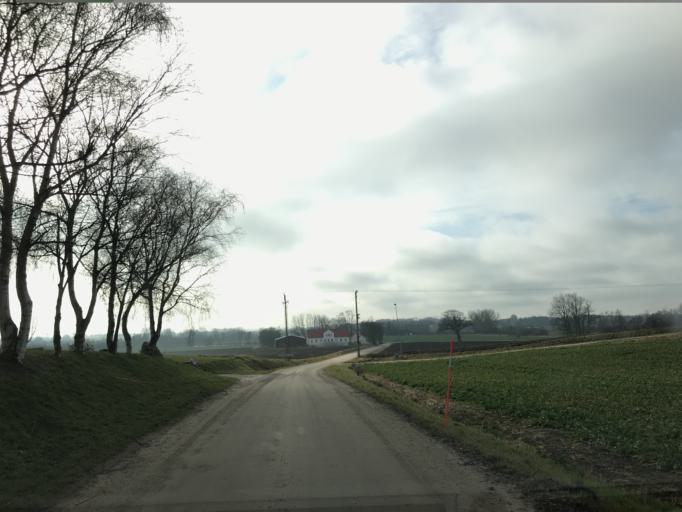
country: SE
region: Skane
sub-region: Svalovs Kommun
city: Teckomatorp
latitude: 55.8259
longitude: 13.0685
